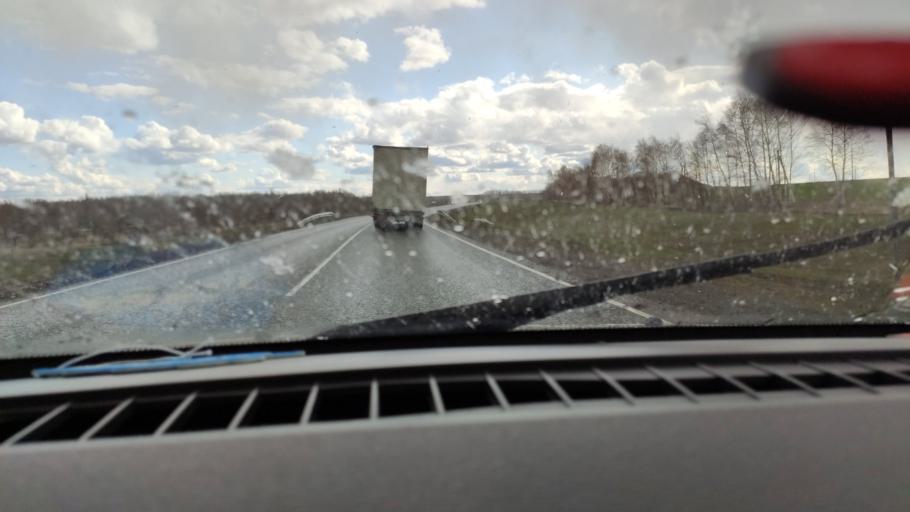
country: RU
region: Saratov
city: Balakovo
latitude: 52.1099
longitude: 47.7476
